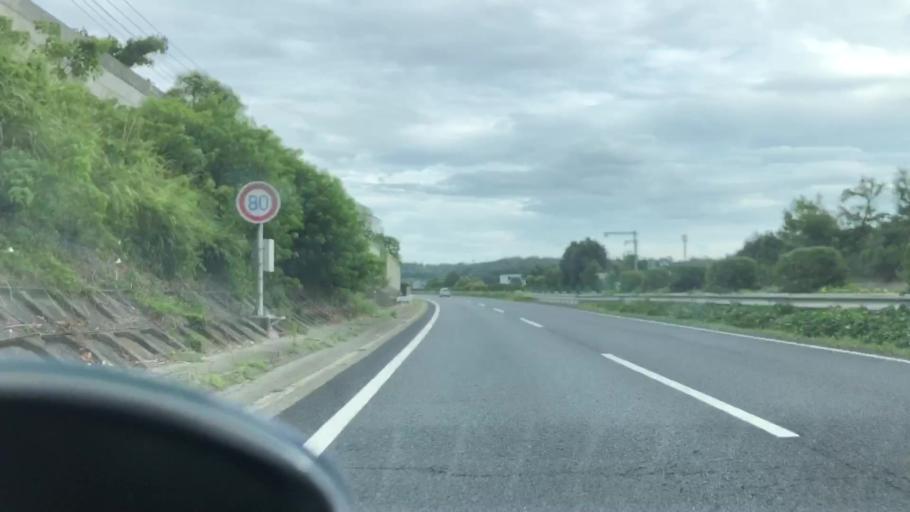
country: JP
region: Hyogo
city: Yashiro
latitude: 34.9217
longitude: 134.9928
